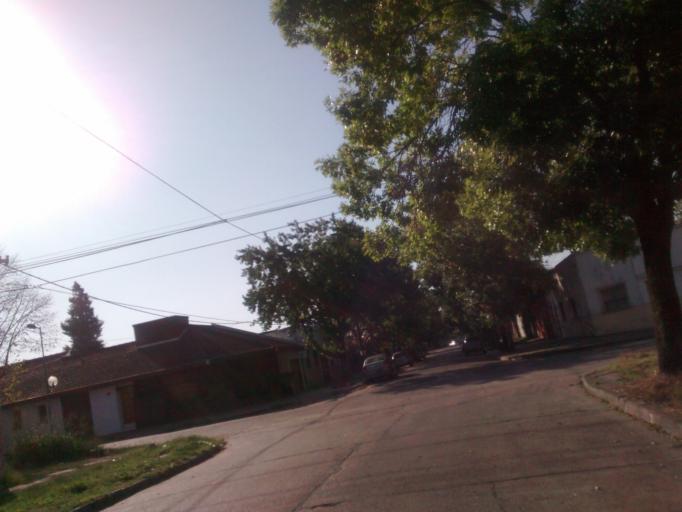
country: AR
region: Buenos Aires
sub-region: Partido de La Plata
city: La Plata
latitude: -34.9211
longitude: -57.9207
